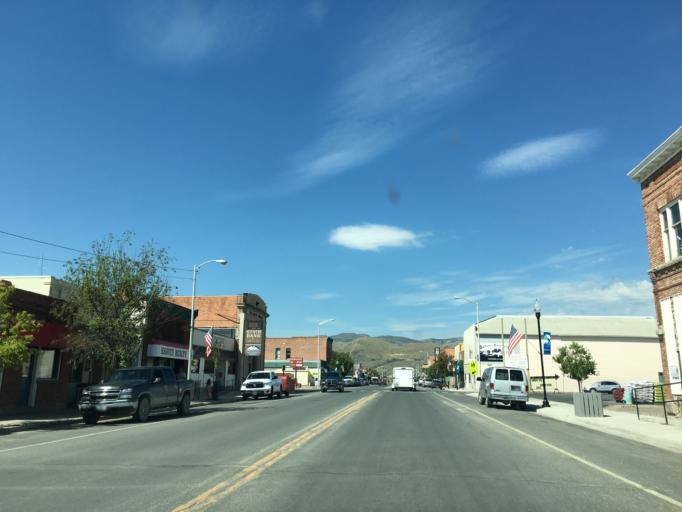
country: US
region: Montana
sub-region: Broadwater County
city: Townsend
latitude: 46.3208
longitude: -111.5166
